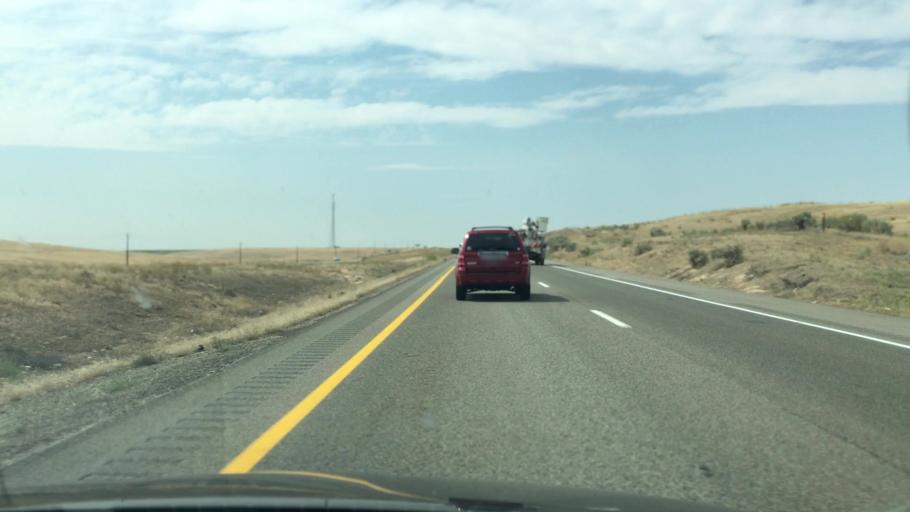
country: US
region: Idaho
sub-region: Ada County
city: Boise
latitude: 43.4431
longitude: -116.0701
